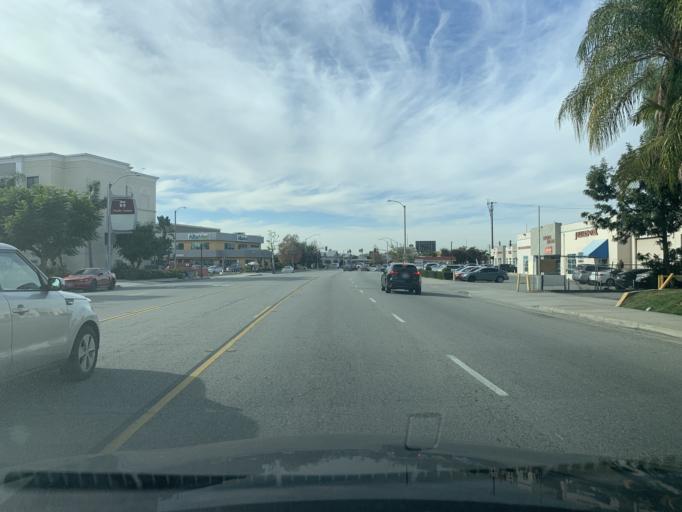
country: US
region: California
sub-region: Los Angeles County
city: El Monte
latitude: 34.0765
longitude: -118.0446
